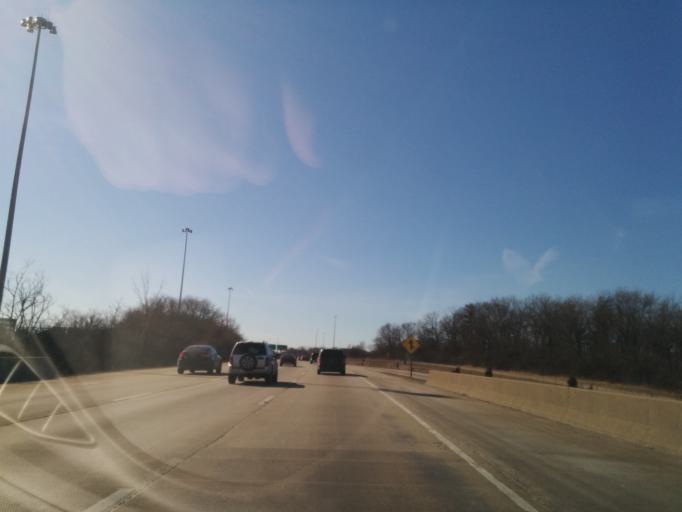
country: US
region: Illinois
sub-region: Cook County
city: Indian Head Park
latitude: 41.7603
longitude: -87.9080
